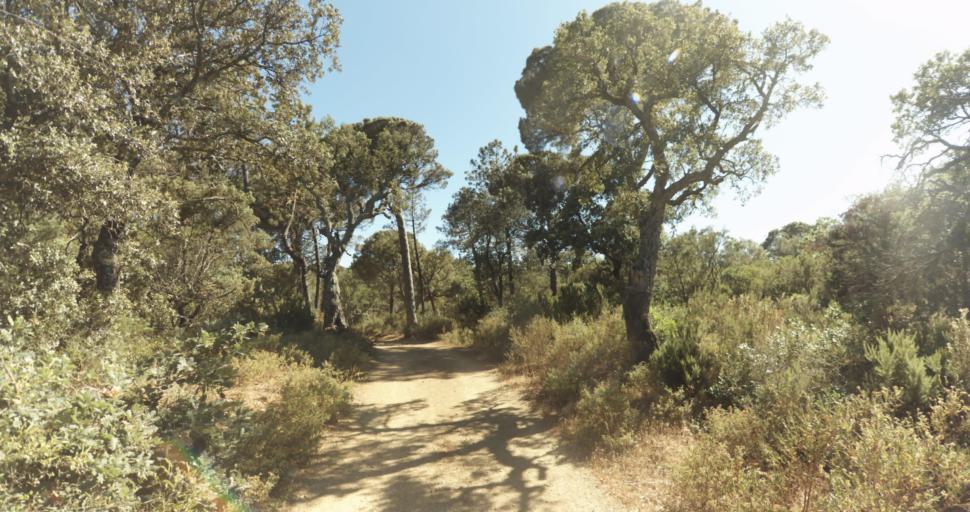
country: FR
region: Provence-Alpes-Cote d'Azur
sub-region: Departement du Var
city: Gassin
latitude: 43.2480
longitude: 6.5847
